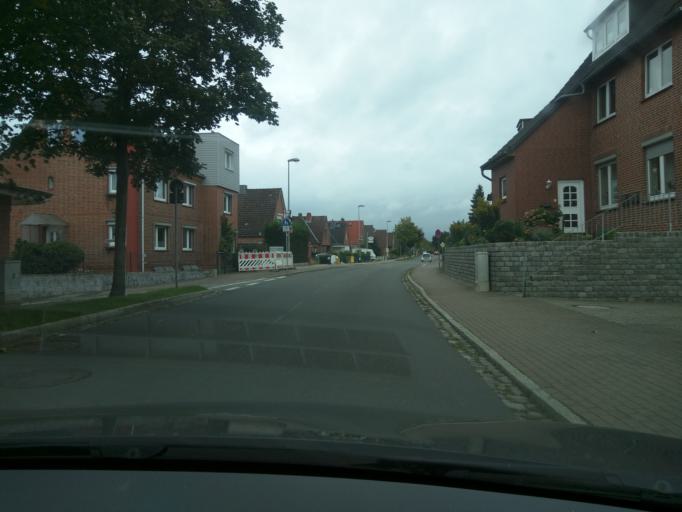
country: DE
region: Schleswig-Holstein
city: Lauenburg
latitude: 53.3792
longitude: 10.5551
